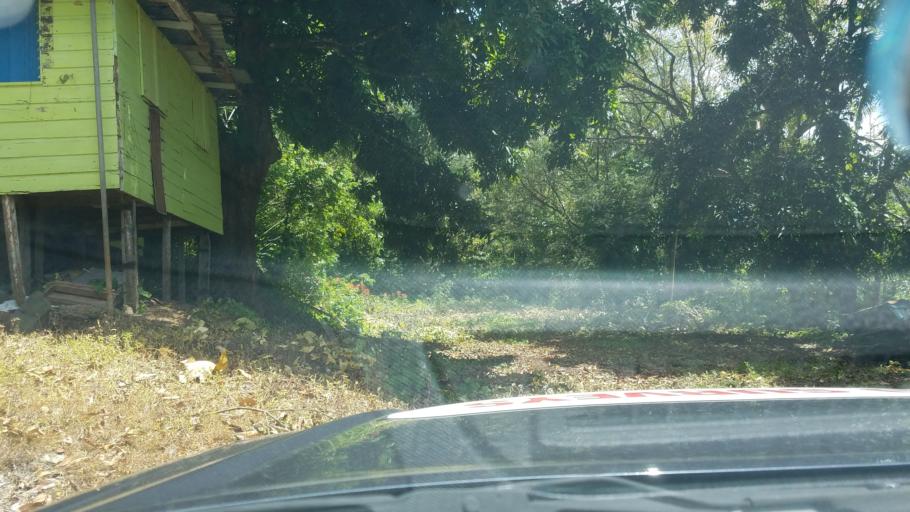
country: LC
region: Castries Quarter
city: Bisee
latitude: 14.0287
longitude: -60.9518
